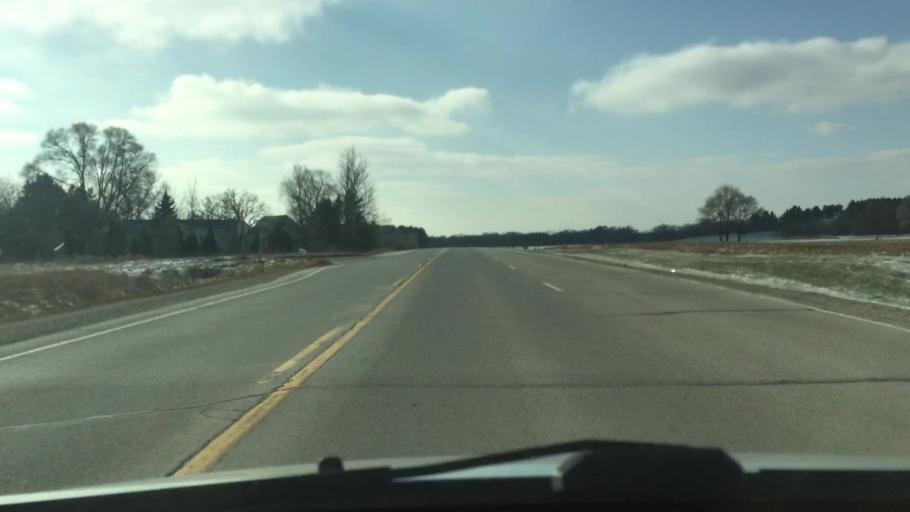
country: US
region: Wisconsin
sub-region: Waukesha County
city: North Prairie
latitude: 42.9214
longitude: -88.4333
